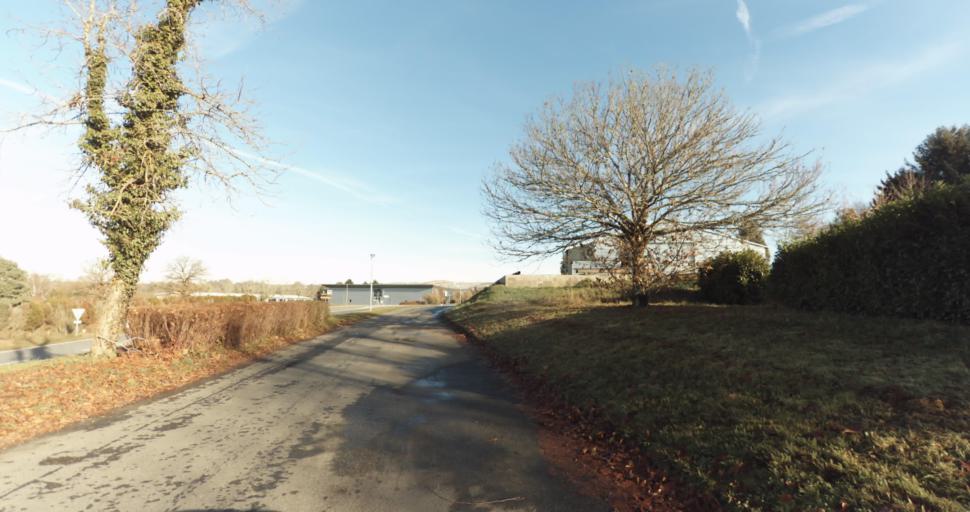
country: FR
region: Limousin
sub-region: Departement de la Haute-Vienne
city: Saint-Priest-sous-Aixe
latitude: 45.8009
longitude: 1.1121
